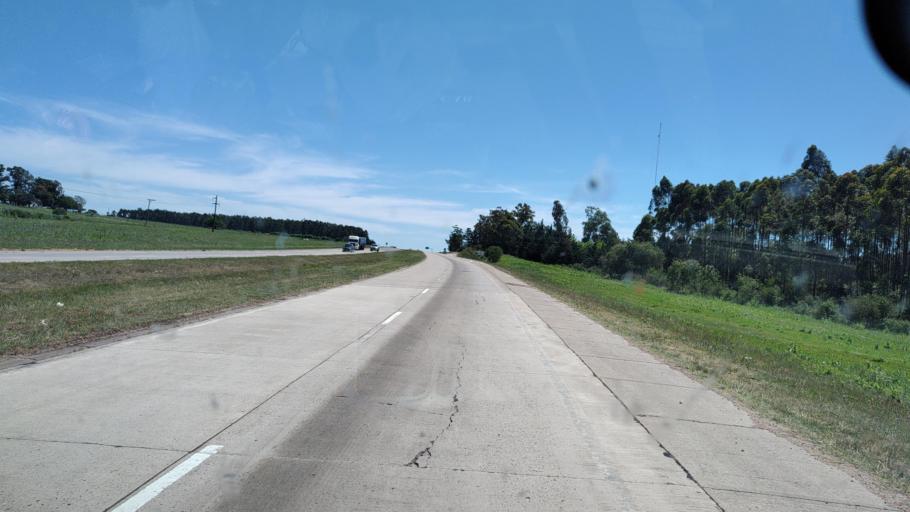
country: AR
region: Entre Rios
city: Villa Elisa
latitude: -32.0807
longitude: -58.2509
